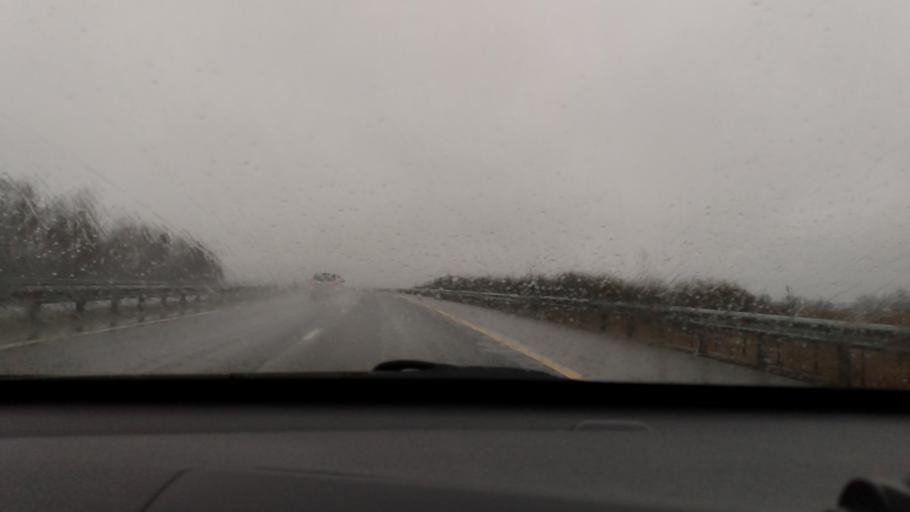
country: RU
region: Tula
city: Gritsovskiy
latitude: 54.2367
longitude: 38.1276
